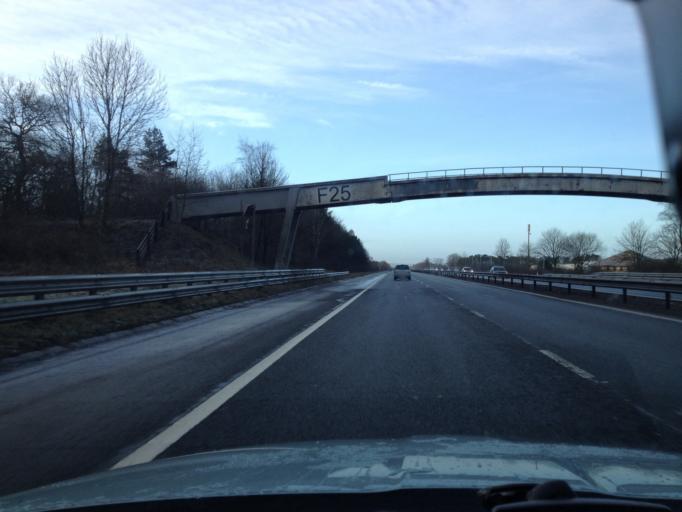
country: GB
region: Scotland
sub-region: West Lothian
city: Livingston
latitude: 55.9115
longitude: -3.5601
